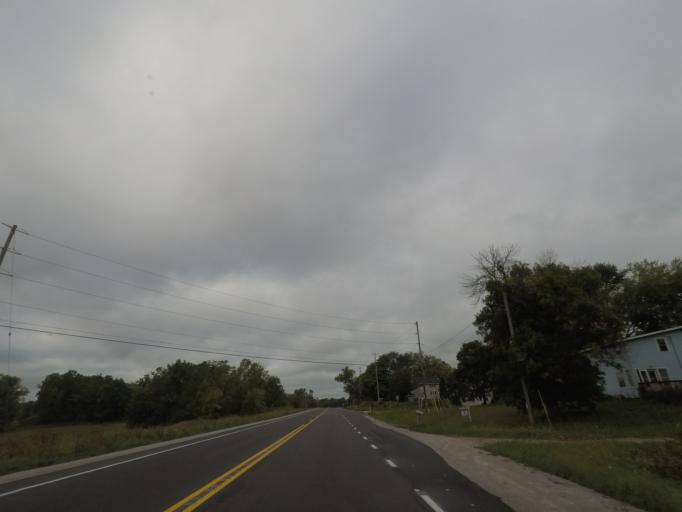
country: US
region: Wisconsin
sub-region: Jefferson County
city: Johnson Creek
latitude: 43.0172
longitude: -88.7378
